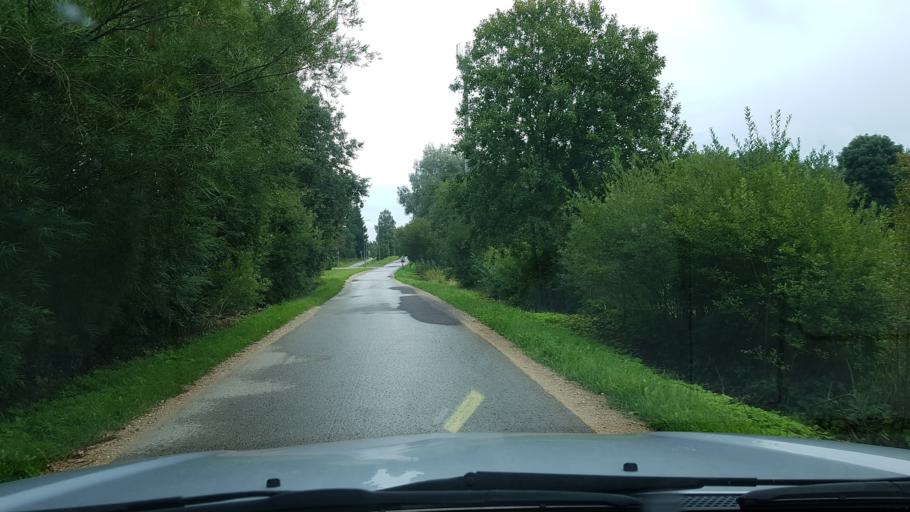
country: EE
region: Harju
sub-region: Rae vald
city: Jueri
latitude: 59.3737
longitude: 24.9379
